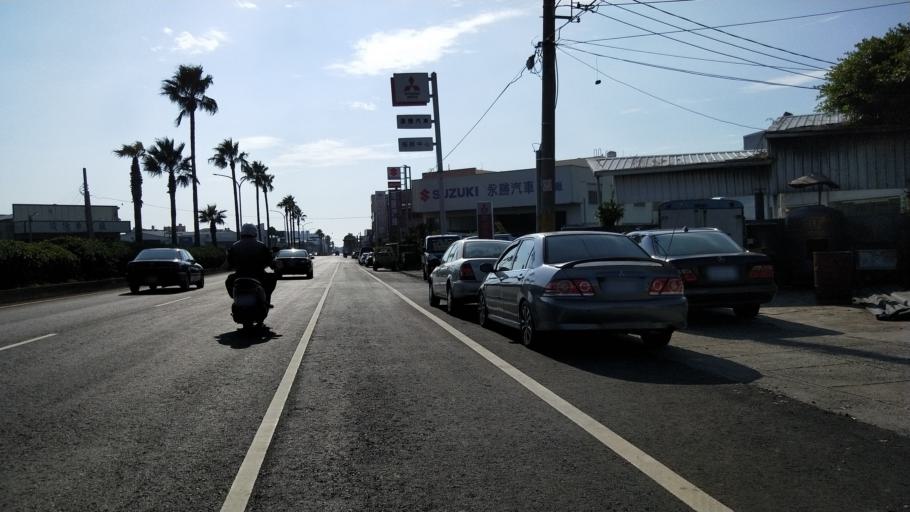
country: TW
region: Taiwan
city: Fengyuan
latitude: 24.3621
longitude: 120.6360
